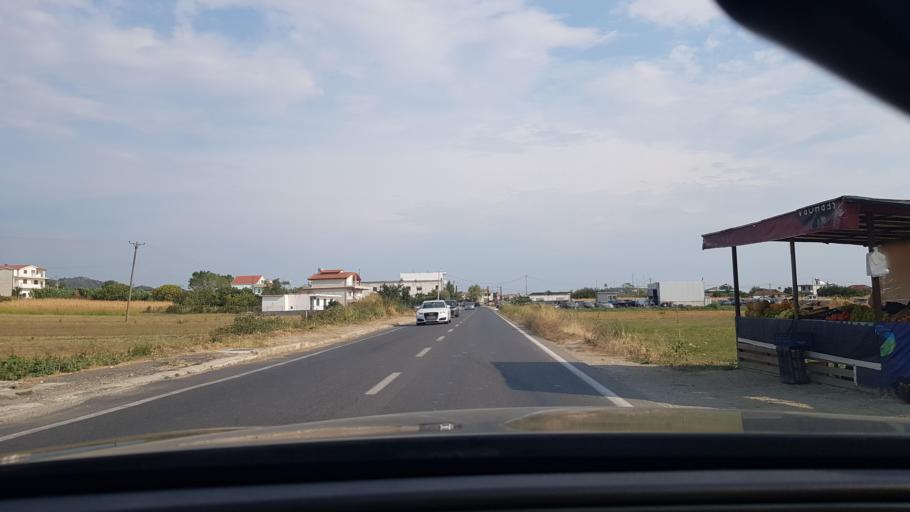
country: AL
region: Durres
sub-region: Rrethi i Durresit
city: Manze
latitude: 41.4524
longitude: 19.5692
